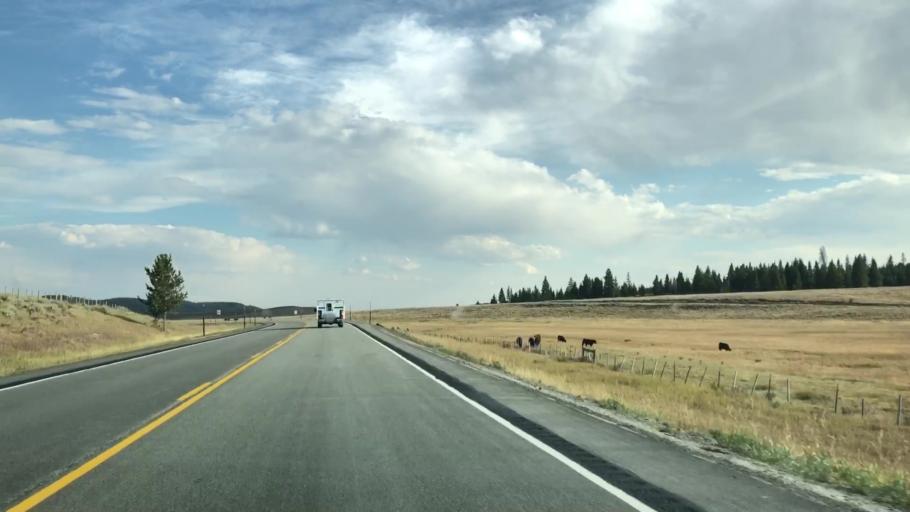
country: US
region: Wyoming
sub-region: Sublette County
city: Pinedale
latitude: 43.1278
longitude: -110.1902
